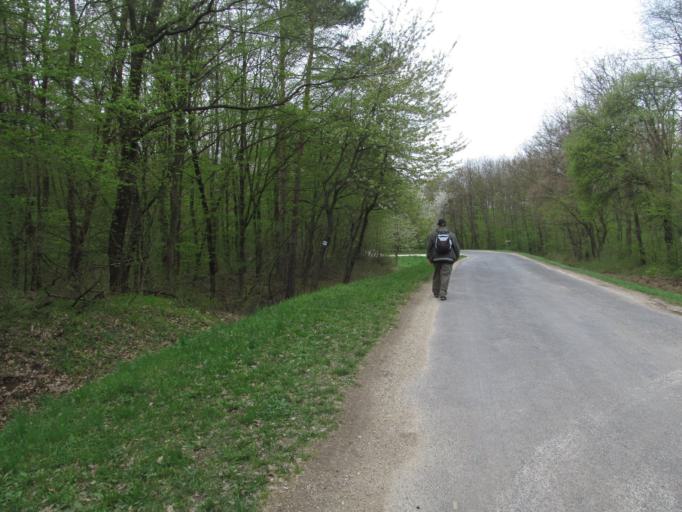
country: HU
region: Veszprem
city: Zanka
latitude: 46.9656
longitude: 17.6584
